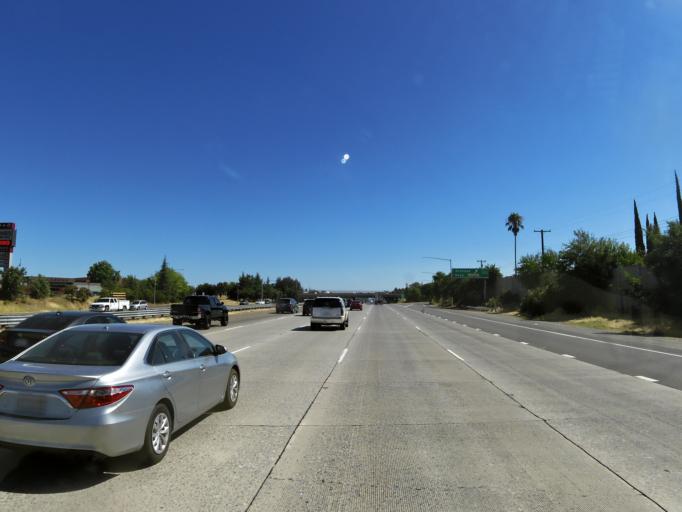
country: US
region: California
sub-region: Sacramento County
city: Antelope
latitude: 38.7044
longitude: -121.3126
